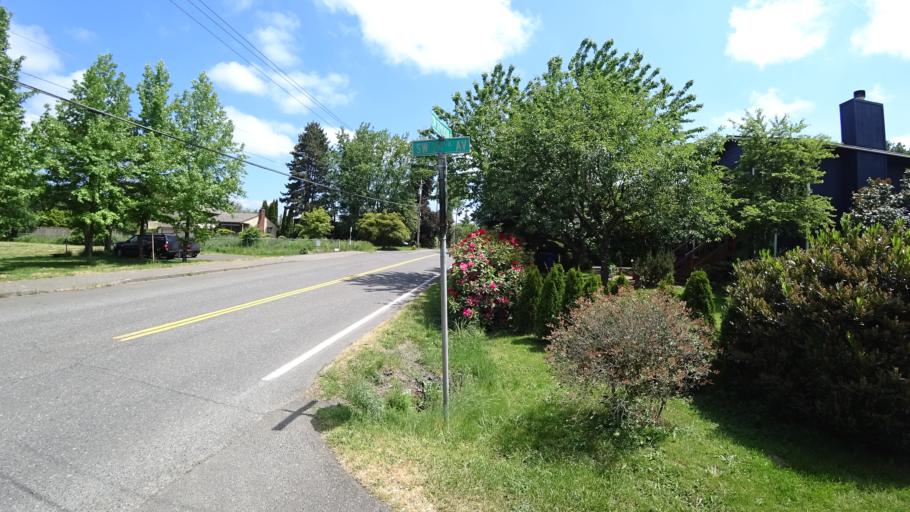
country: US
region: Oregon
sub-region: Clackamas County
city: Lake Oswego
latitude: 45.4401
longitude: -122.7029
